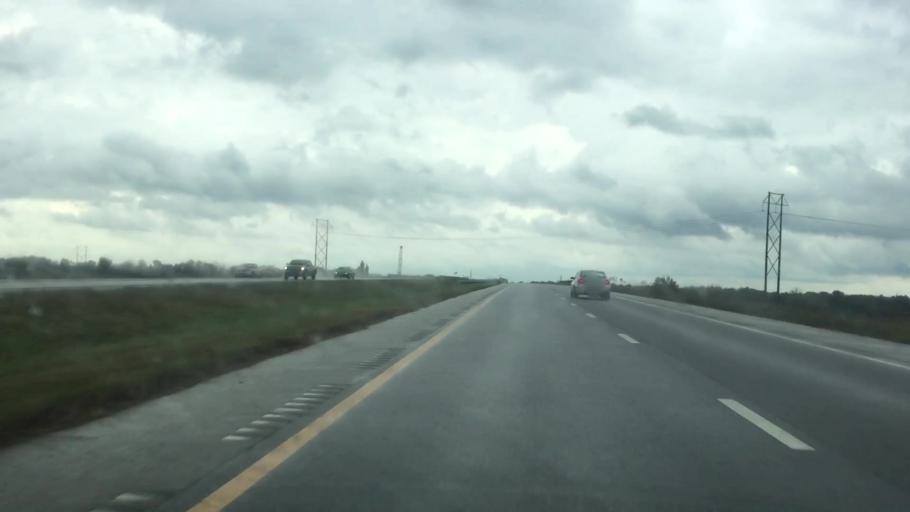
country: US
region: Kansas
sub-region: Miami County
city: Osawatomie
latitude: 38.5208
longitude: -94.9095
